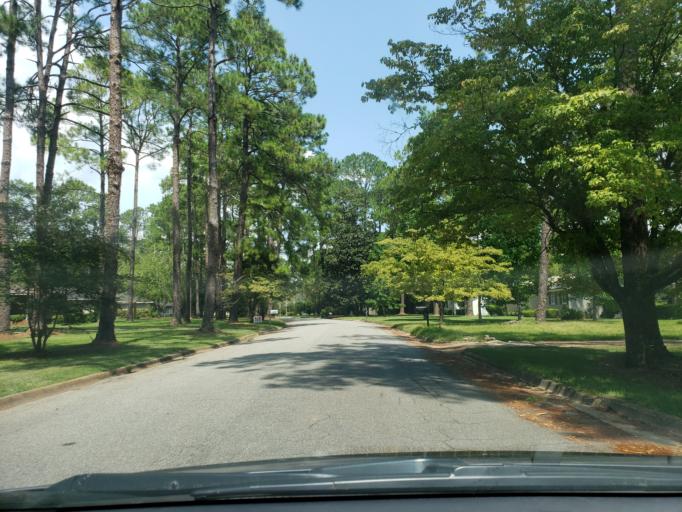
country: US
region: Georgia
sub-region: Dougherty County
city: Albany
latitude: 31.5953
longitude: -84.2003
